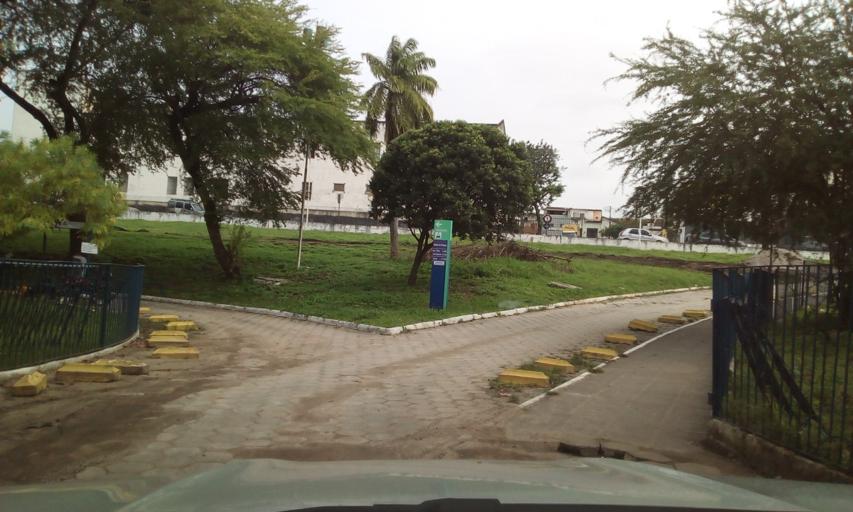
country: BR
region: Paraiba
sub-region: Joao Pessoa
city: Joao Pessoa
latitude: -7.1193
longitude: -34.8910
